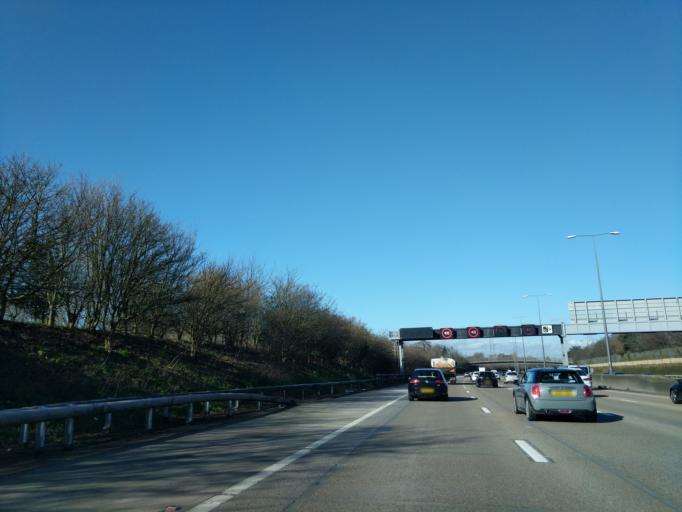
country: GB
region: England
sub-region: Surrey
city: Byfleet
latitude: 51.3308
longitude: -0.4806
